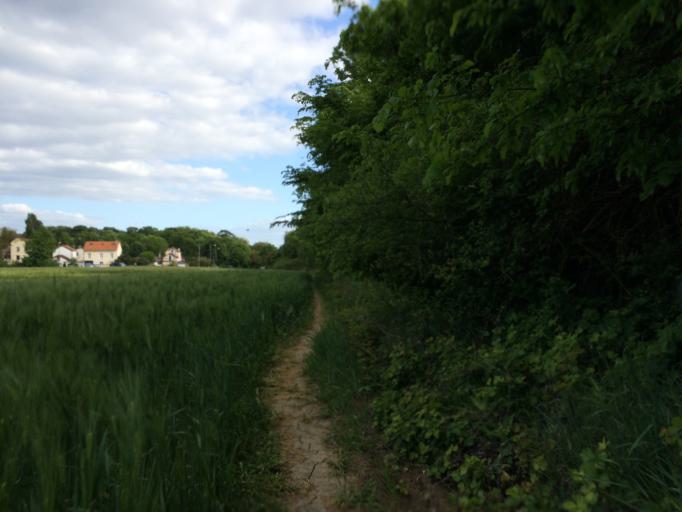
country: FR
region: Ile-de-France
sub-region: Departement de l'Essonne
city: Ris-Orangis
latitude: 48.6637
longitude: 2.4142
